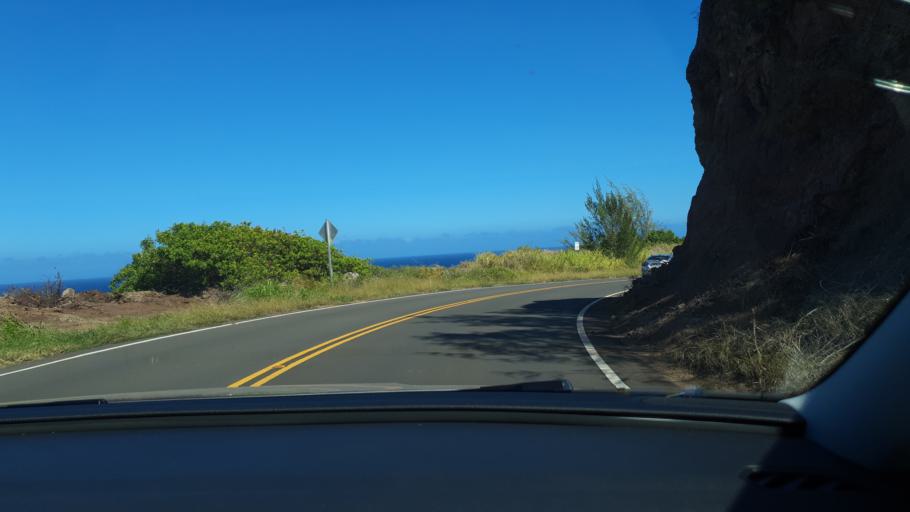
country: US
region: Hawaii
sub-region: Maui County
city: Napili-Honokowai
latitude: 21.0159
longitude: -156.5764
